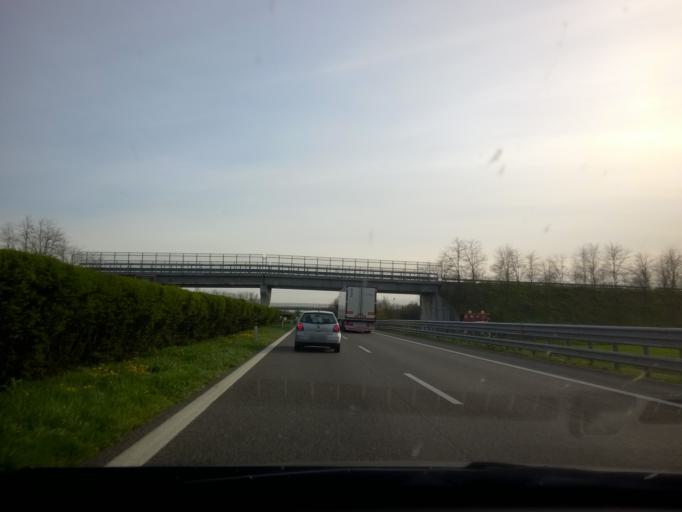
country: IT
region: Lombardy
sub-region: Provincia di Brescia
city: San Gervasio Bresciano
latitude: 45.3139
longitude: 10.1440
